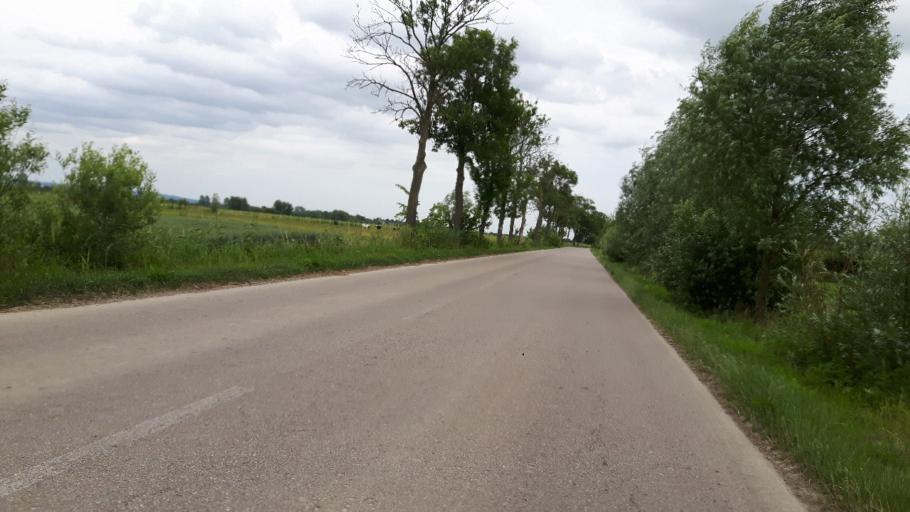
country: PL
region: Warmian-Masurian Voivodeship
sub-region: Powiat elblaski
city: Gronowo Elblaskie
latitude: 54.1984
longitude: 19.2889
